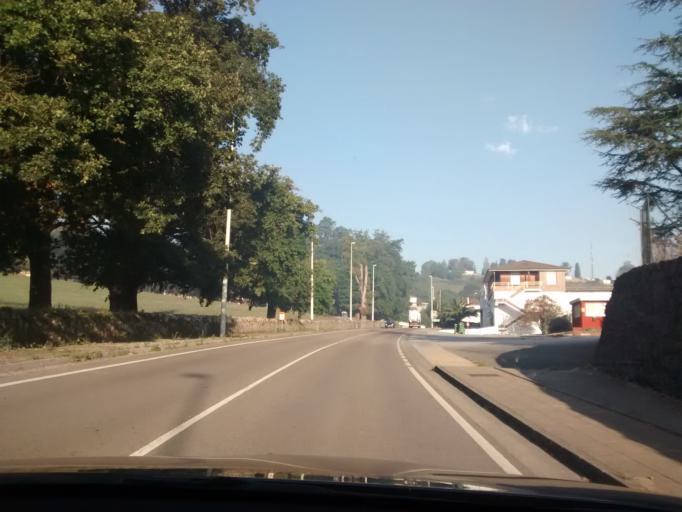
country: ES
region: Cantabria
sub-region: Provincia de Cantabria
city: Lierganes
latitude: 43.3794
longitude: -3.7289
